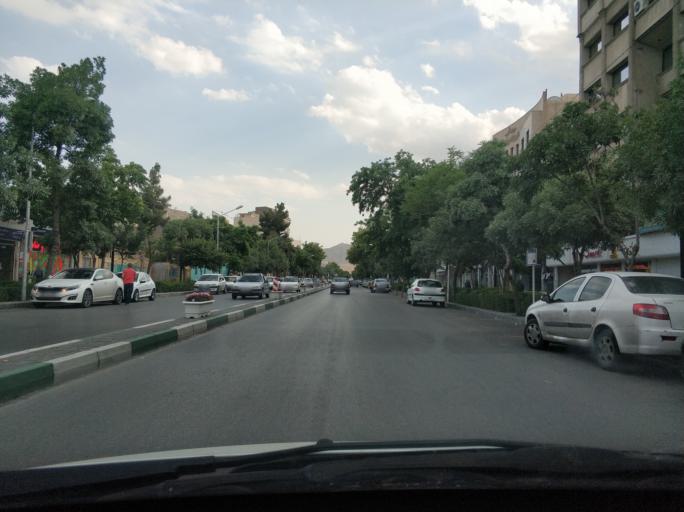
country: IR
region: Razavi Khorasan
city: Mashhad
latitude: 36.2836
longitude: 59.5972
